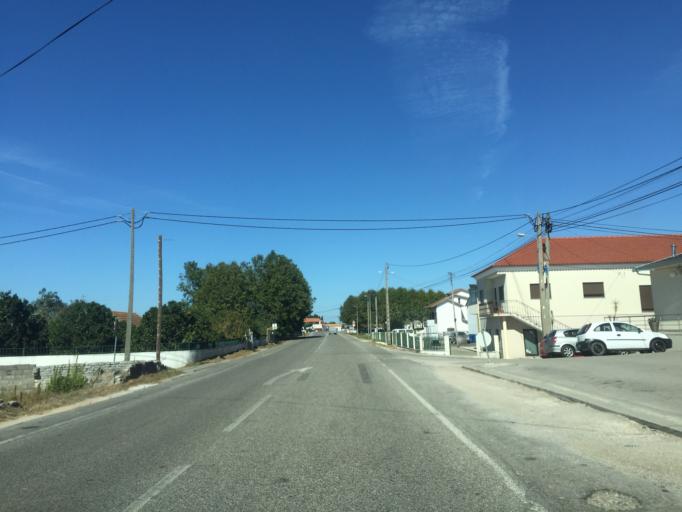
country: PT
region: Coimbra
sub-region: Figueira da Foz
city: Alhadas
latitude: 40.2634
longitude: -8.7796
